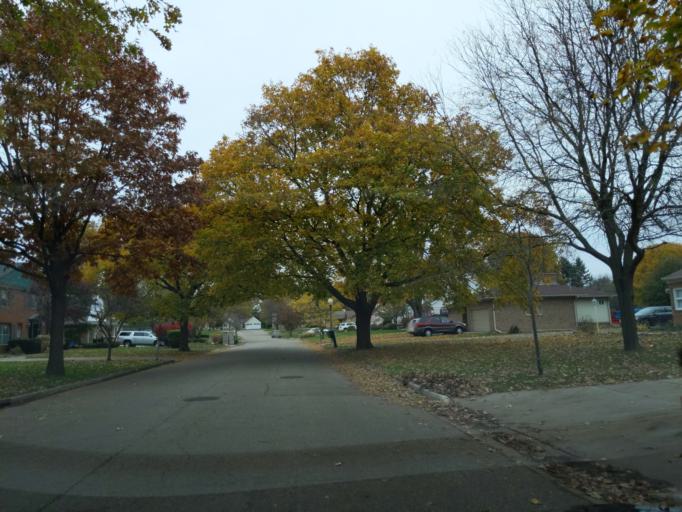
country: US
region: Michigan
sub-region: Ingham County
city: Edgemont Park
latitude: 42.7135
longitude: -84.5878
